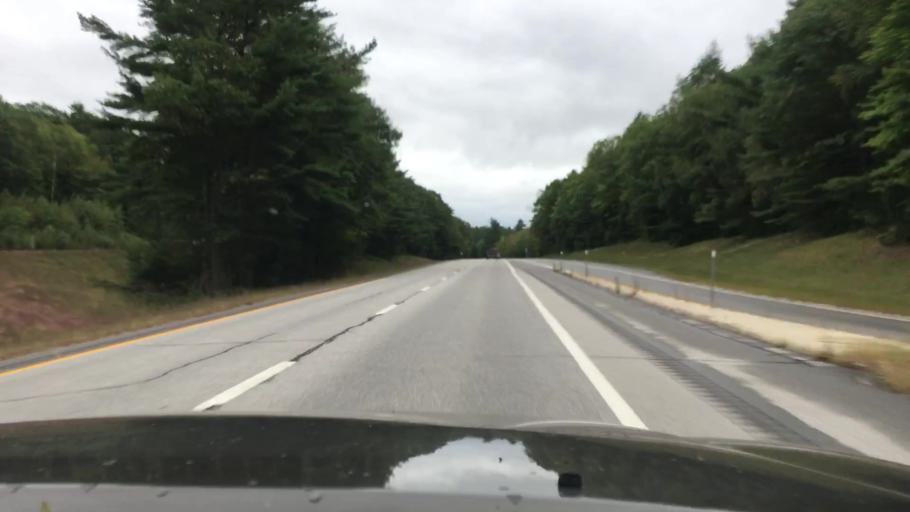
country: US
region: New Hampshire
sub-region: Belknap County
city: Sanbornton
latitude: 43.5023
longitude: -71.6136
